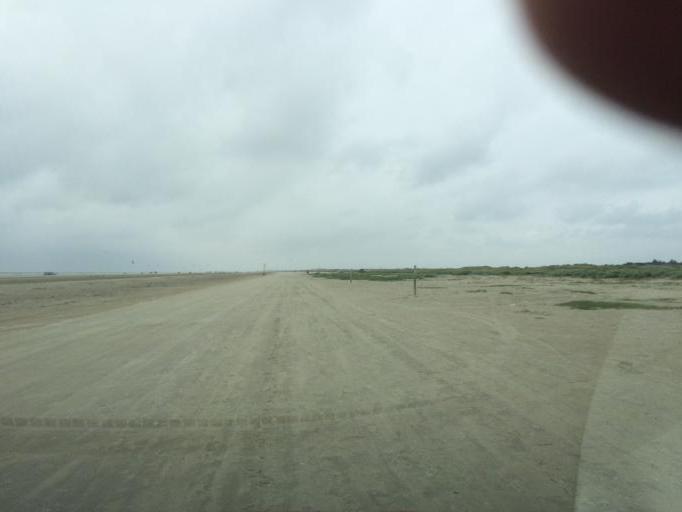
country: DK
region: South Denmark
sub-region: Fano Kommune
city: Nordby
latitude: 55.3865
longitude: 8.4022
